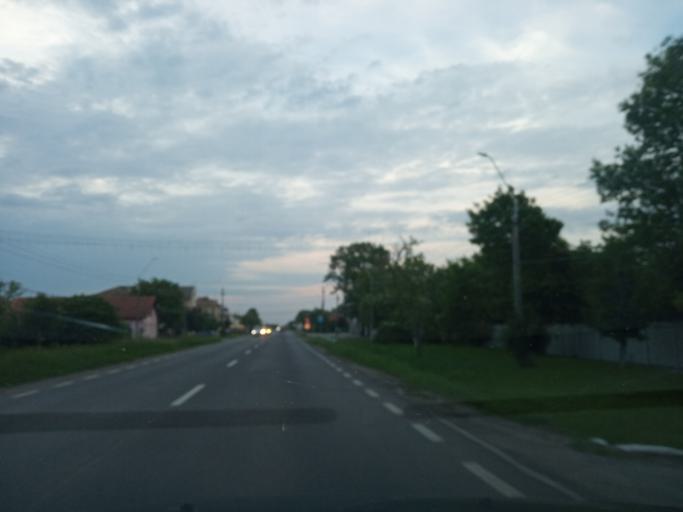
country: RO
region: Timis
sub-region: Comuna Voiteg
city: Voiteg
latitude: 45.4691
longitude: 21.2349
